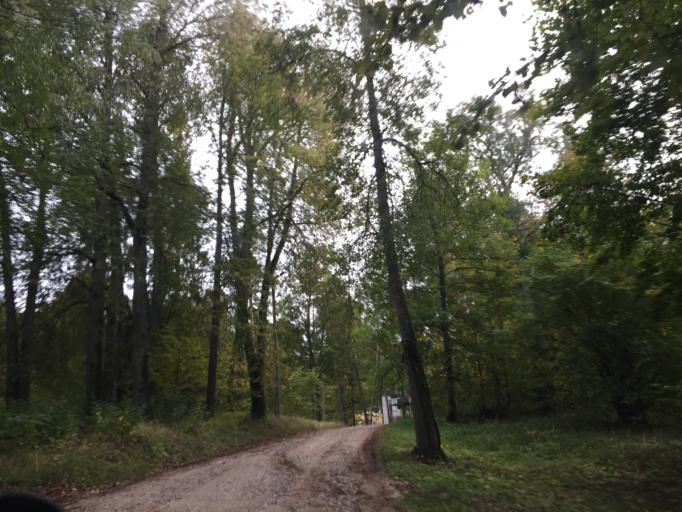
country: LV
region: Auces Novads
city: Auce
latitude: 56.5520
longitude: 23.0174
